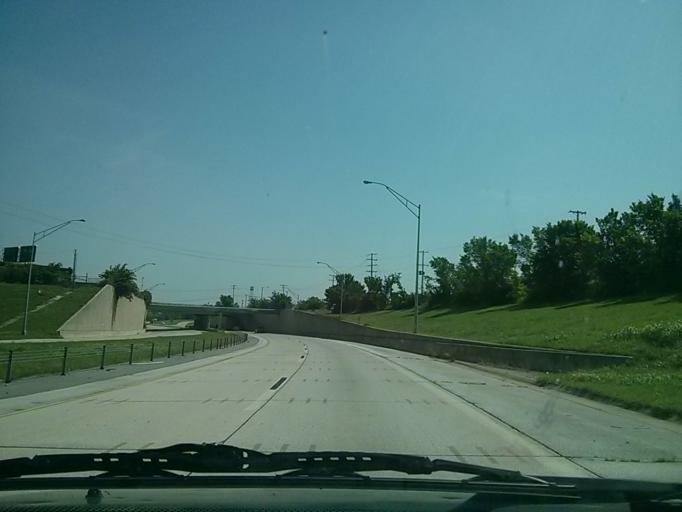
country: US
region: Oklahoma
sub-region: Tulsa County
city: Oakhurst
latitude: 36.1030
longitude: -96.0225
